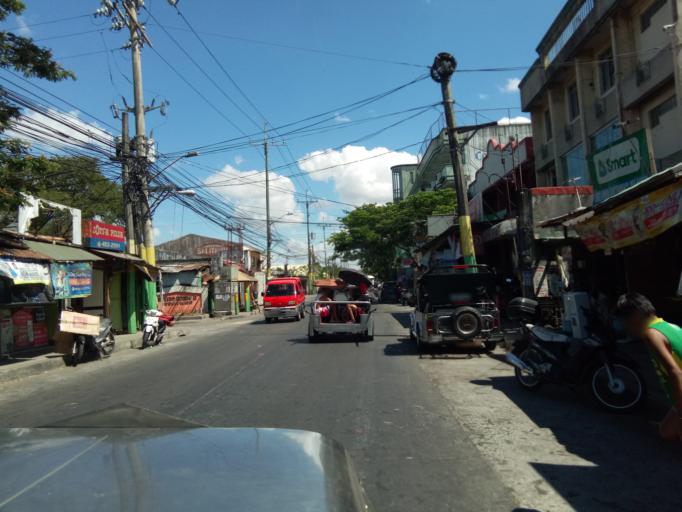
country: PH
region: Calabarzon
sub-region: Province of Cavite
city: Dasmarinas
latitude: 14.3437
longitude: 120.9471
